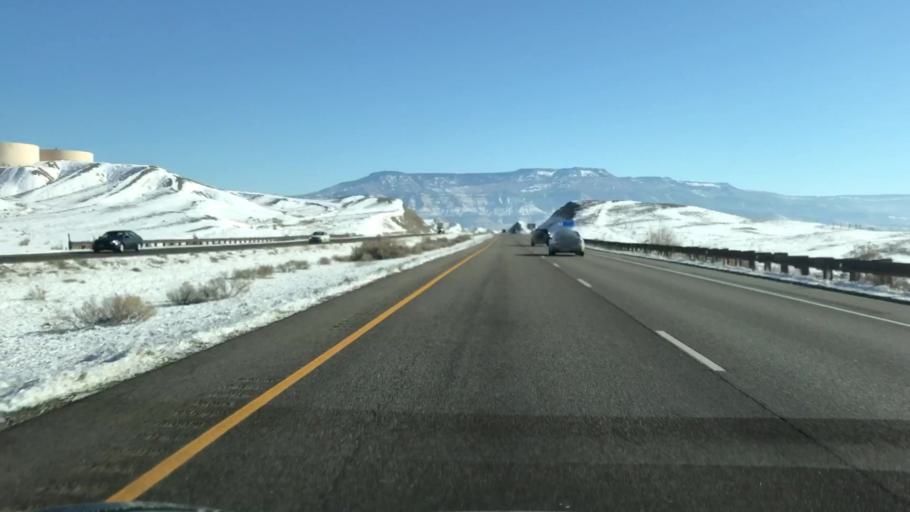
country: US
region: Colorado
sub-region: Mesa County
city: Clifton
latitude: 39.1040
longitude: -108.4667
